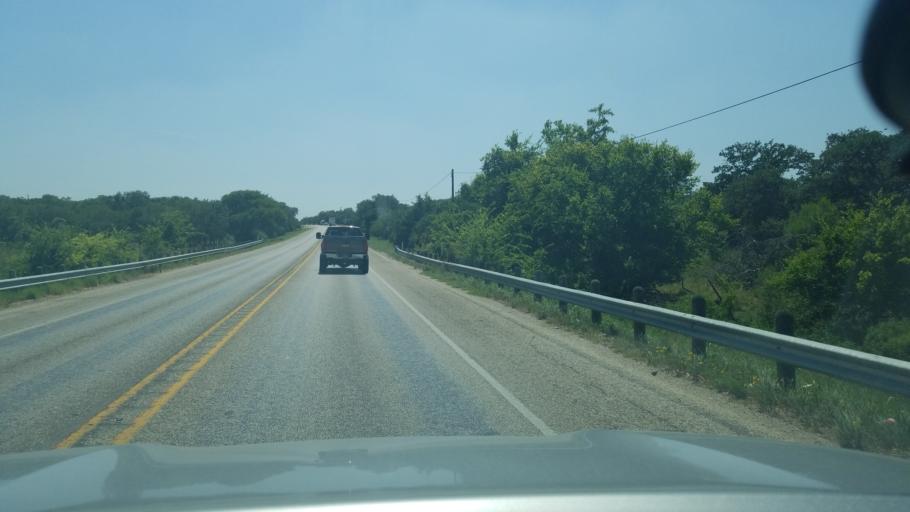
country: US
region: Texas
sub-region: Kendall County
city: Boerne
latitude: 29.7935
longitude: -98.6762
